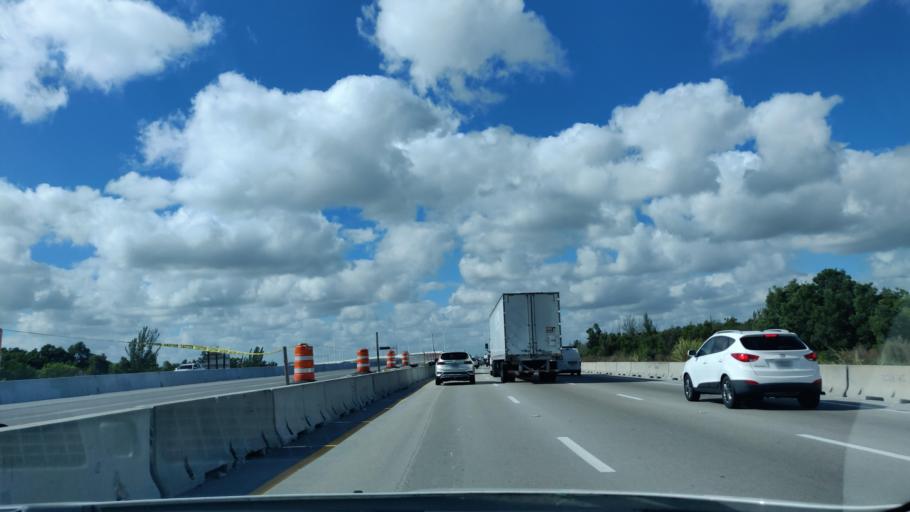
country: US
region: Florida
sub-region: Miami-Dade County
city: Palm Springs North
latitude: 25.9338
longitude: -80.3711
